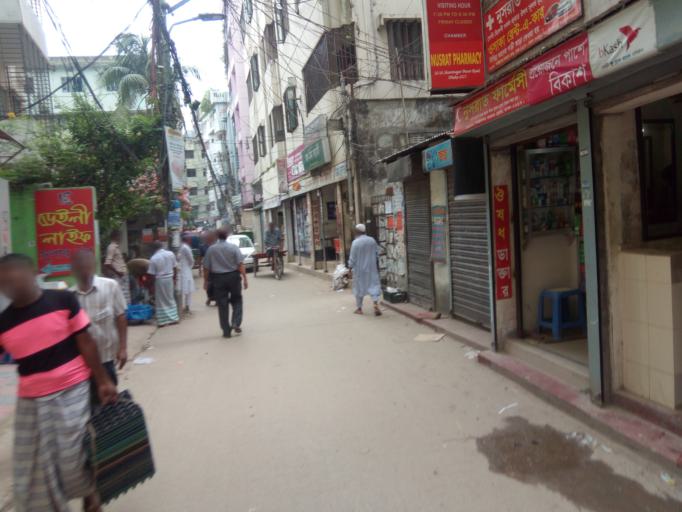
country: BD
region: Dhaka
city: Paltan
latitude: 23.7394
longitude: 90.4114
